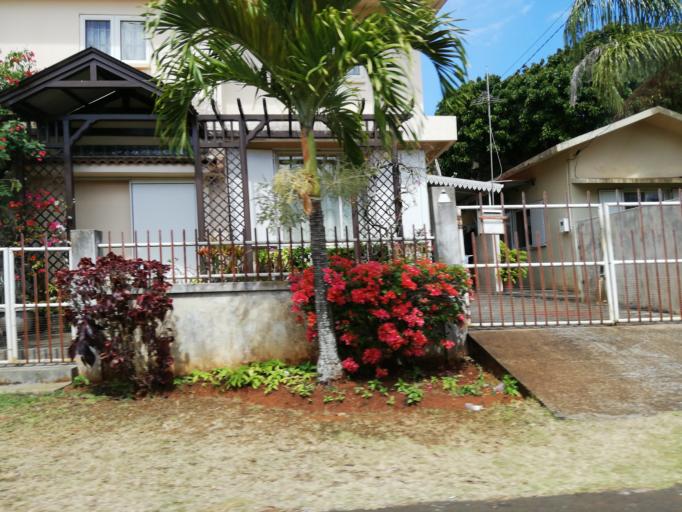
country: MU
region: Moka
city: Moka
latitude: -20.2123
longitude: 57.4735
